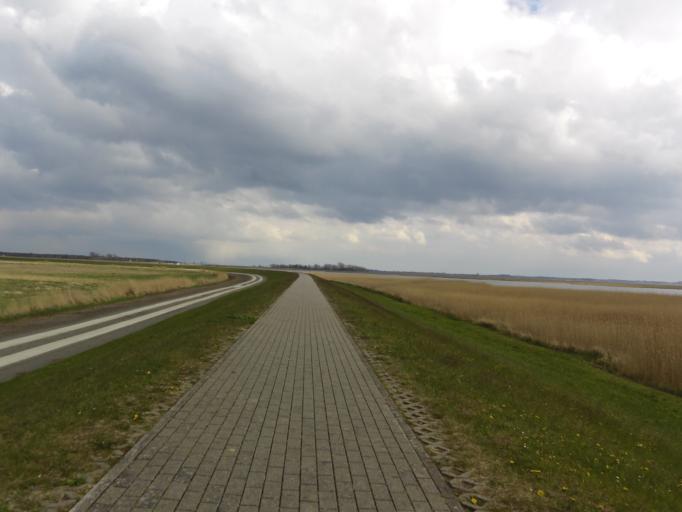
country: DE
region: Mecklenburg-Vorpommern
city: Zingst
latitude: 54.4297
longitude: 12.7079
